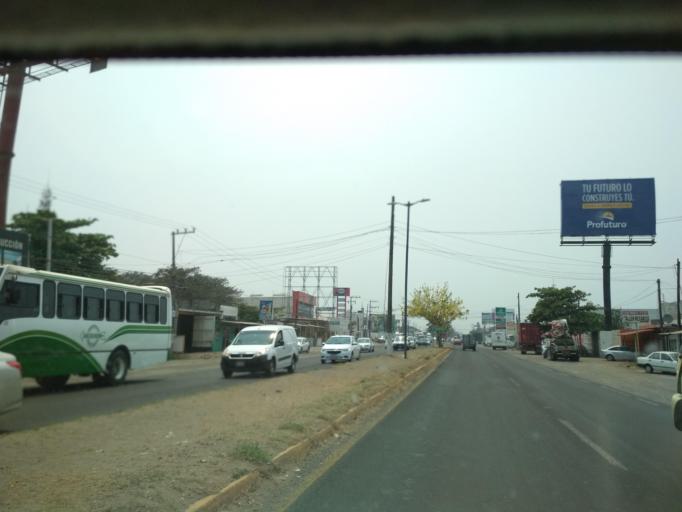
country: MX
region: Veracruz
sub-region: Veracruz
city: Las Amapolas
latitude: 19.1670
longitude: -96.2193
